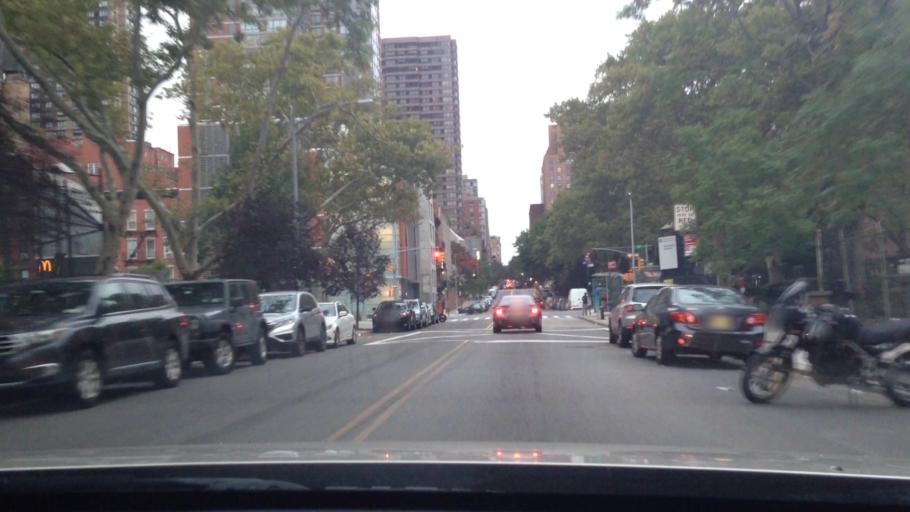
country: US
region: New York
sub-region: New York County
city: Manhattan
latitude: 40.7846
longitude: -73.9457
